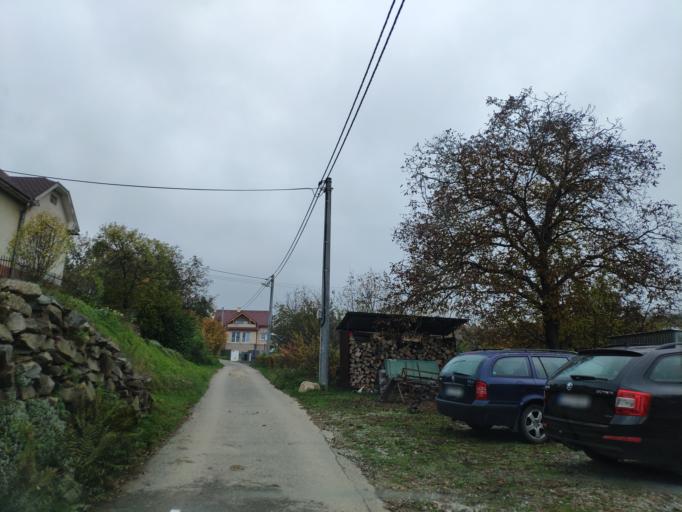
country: SK
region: Kosicky
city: Kosice
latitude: 48.7265
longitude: 21.1081
